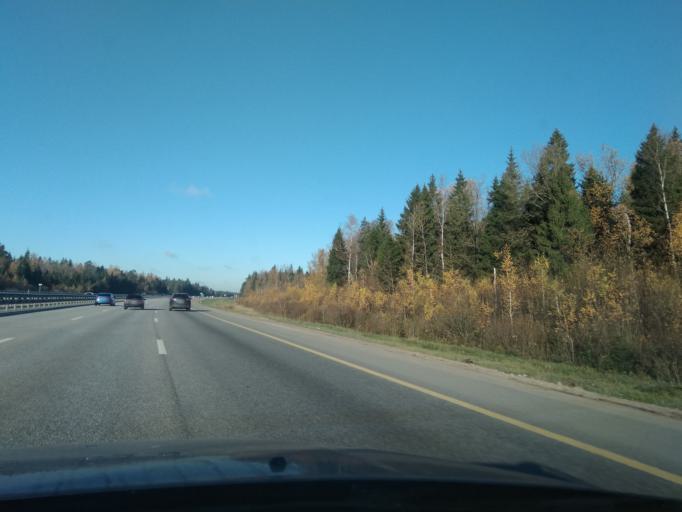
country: RU
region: Moskovskaya
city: Yershovo
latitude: 55.8315
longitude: 36.8564
